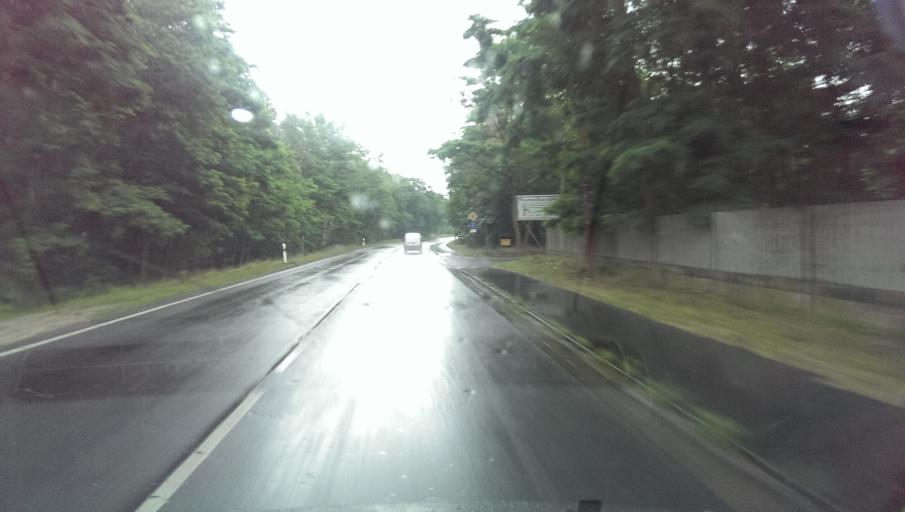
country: DE
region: Brandenburg
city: Premnitz
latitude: 52.5205
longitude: 12.3870
